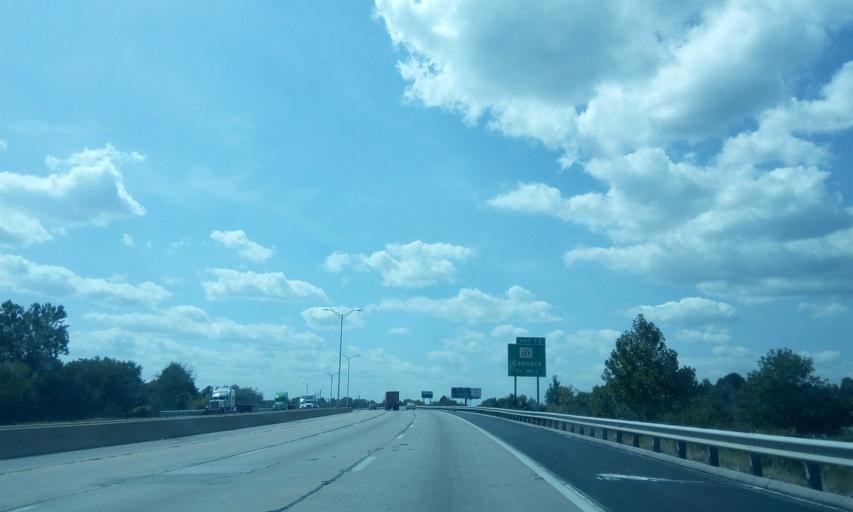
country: US
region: Illinois
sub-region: Saint Clair County
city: Centreville
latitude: 38.5561
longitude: -90.1532
